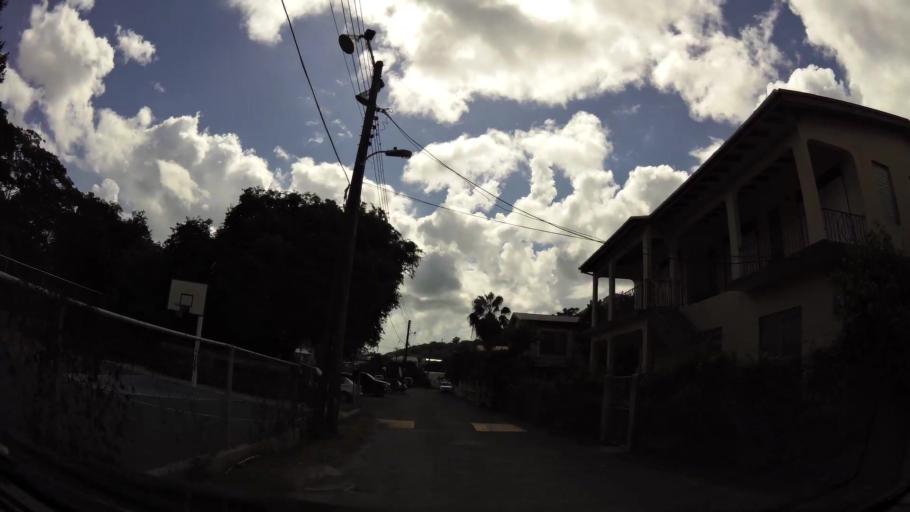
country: VG
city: Road Town
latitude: 18.4275
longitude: -64.6235
